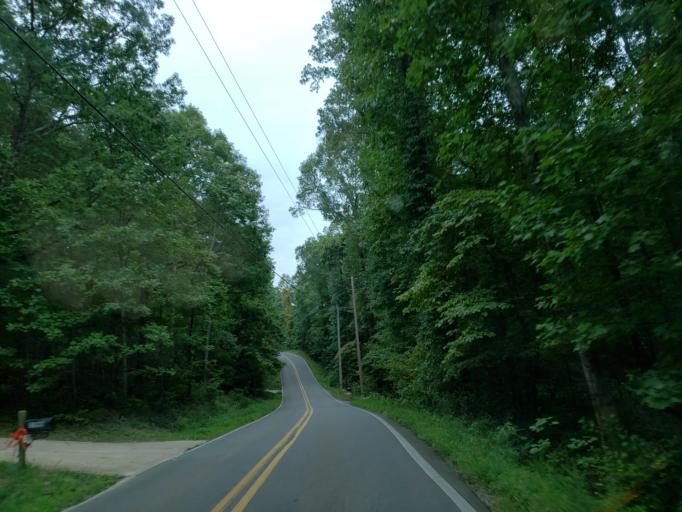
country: US
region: Georgia
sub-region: Pickens County
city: Jasper
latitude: 34.4161
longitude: -84.5356
